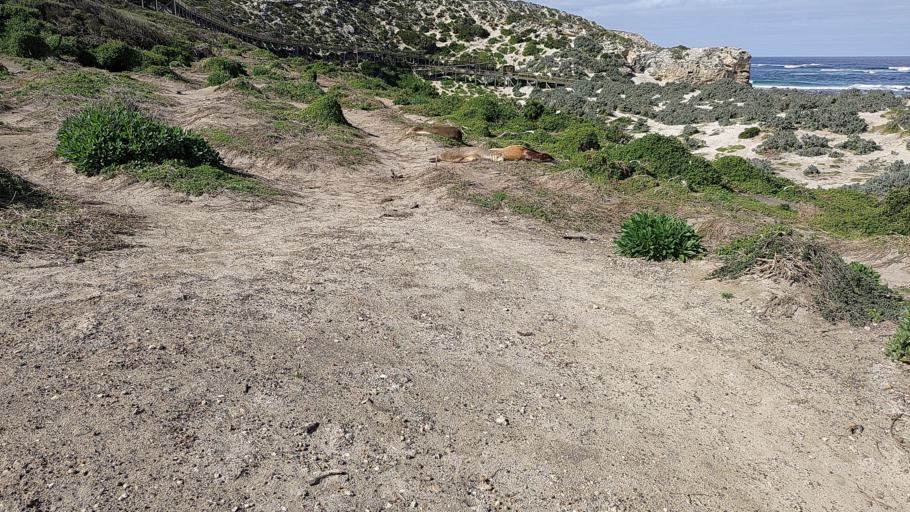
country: AU
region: South Australia
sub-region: Kangaroo Island
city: Kingscote
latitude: -35.9937
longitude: 137.3176
